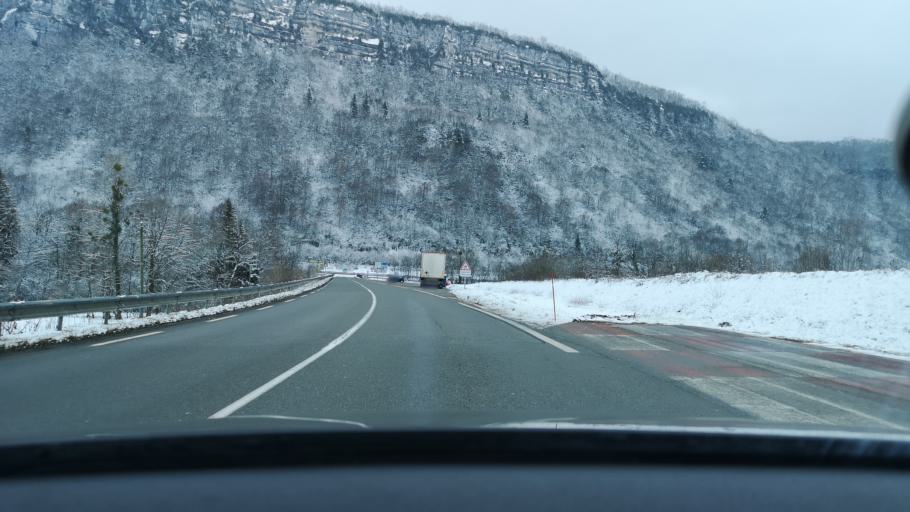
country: FR
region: Rhone-Alpes
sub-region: Departement de l'Ain
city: Dortan
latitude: 46.3646
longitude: 5.7053
